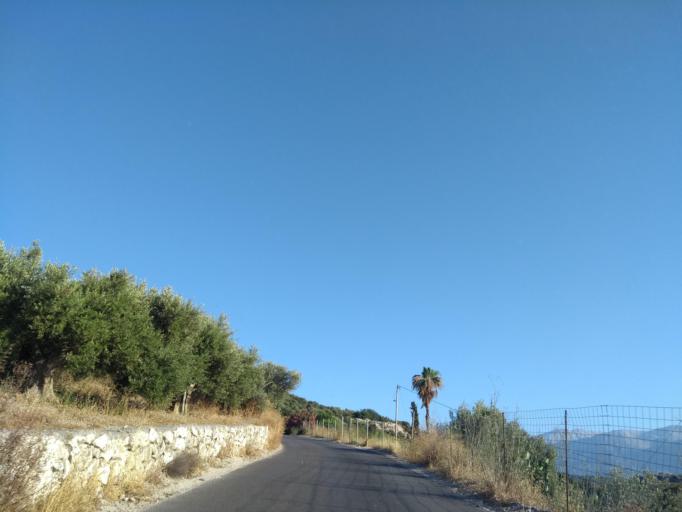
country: GR
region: Crete
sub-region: Nomos Chanias
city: Kalivai
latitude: 35.4414
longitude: 24.1720
